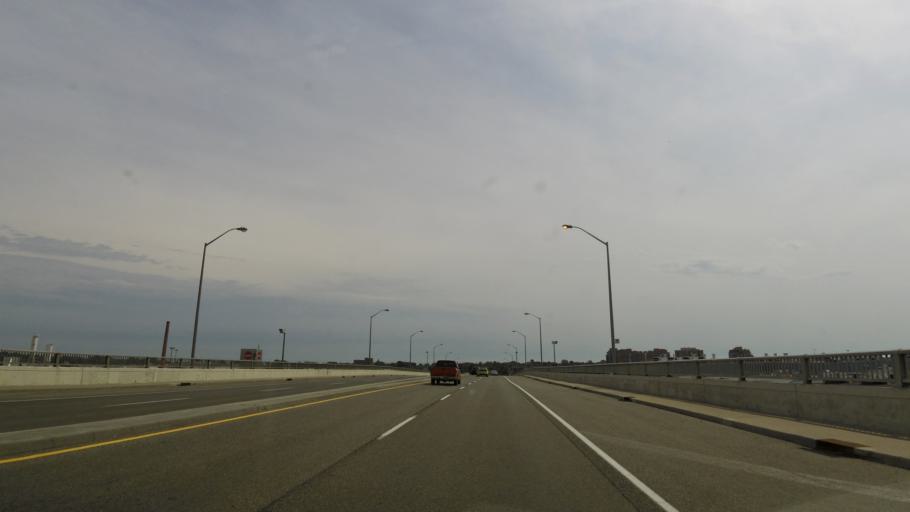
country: CA
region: Ontario
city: Etobicoke
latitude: 43.6104
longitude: -79.5075
